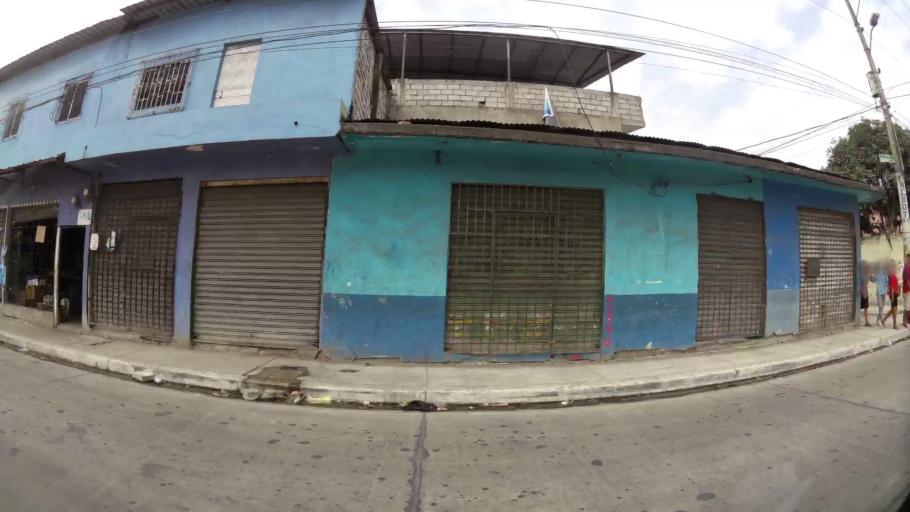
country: EC
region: Guayas
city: Guayaquil
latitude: -2.2470
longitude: -79.9255
